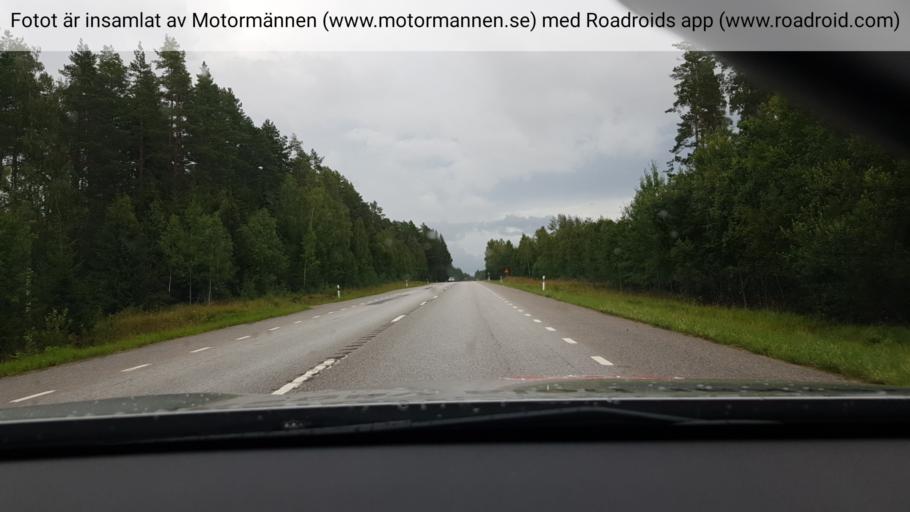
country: SE
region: Uppsala
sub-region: Alvkarleby Kommun
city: AElvkarleby
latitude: 60.5493
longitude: 17.5114
